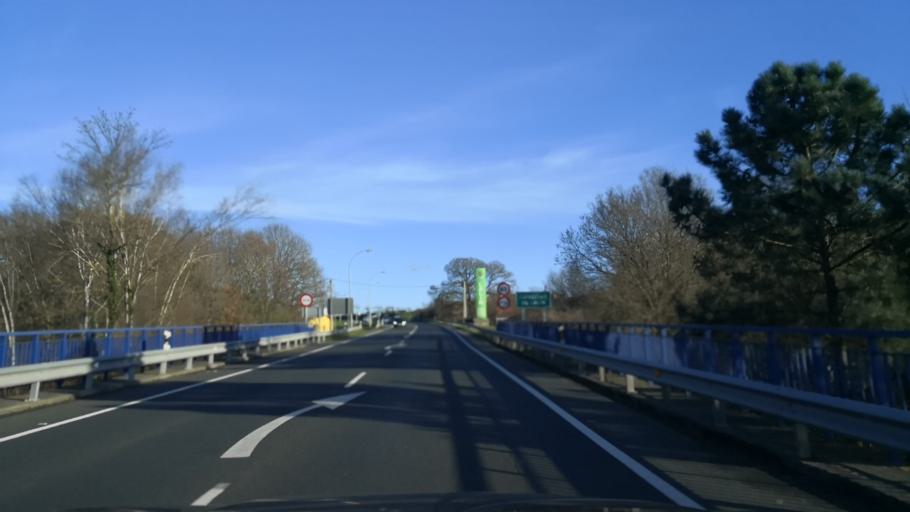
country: ES
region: Galicia
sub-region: Provincia de Pontevedra
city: Silleda
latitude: 42.6843
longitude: -8.1983
